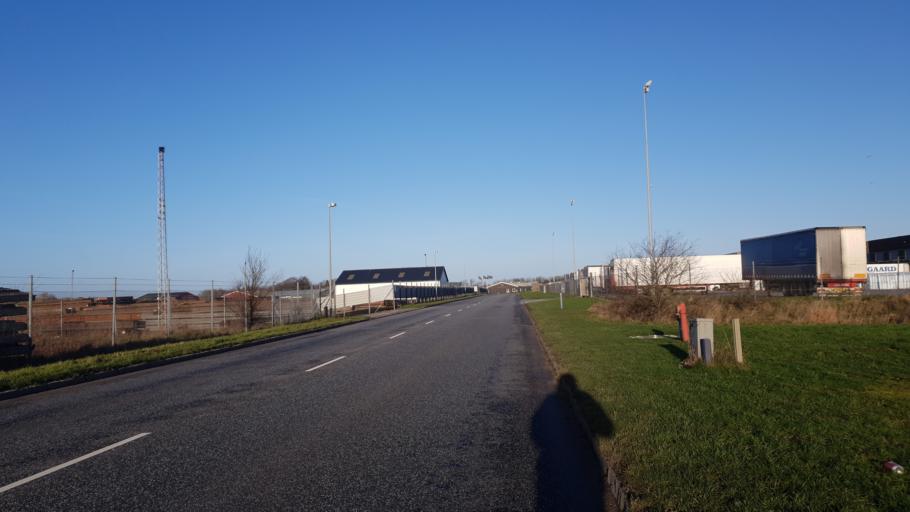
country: DK
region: Central Jutland
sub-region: Hedensted Kommune
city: Hedensted
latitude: 55.7943
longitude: 9.6773
